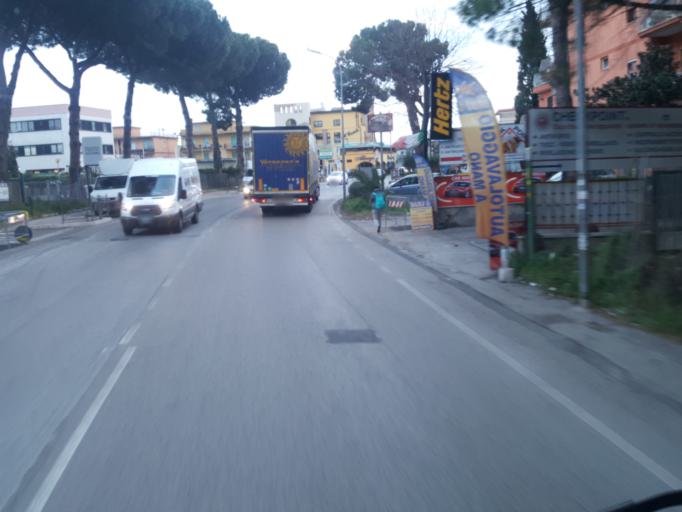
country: IT
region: Latium
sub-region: Citta metropolitana di Roma Capitale
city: Area Produttiva
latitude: 41.6797
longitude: 12.5022
